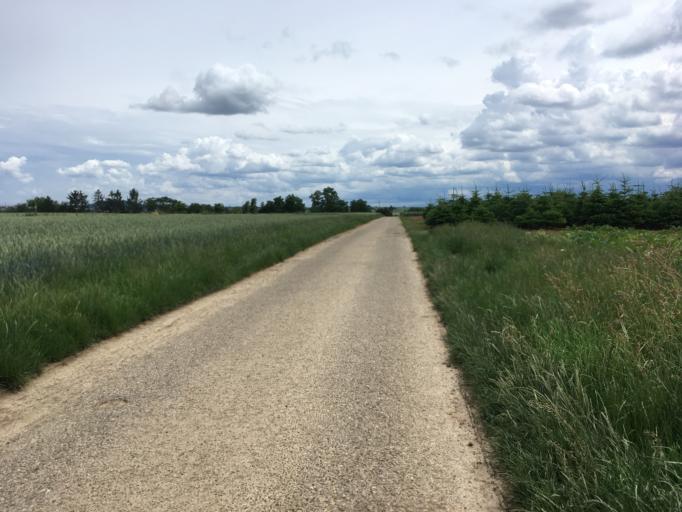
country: DE
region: Baden-Wuerttemberg
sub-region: Regierungsbezirk Stuttgart
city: Bietigheim-Bissingen
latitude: 48.9527
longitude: 9.0941
